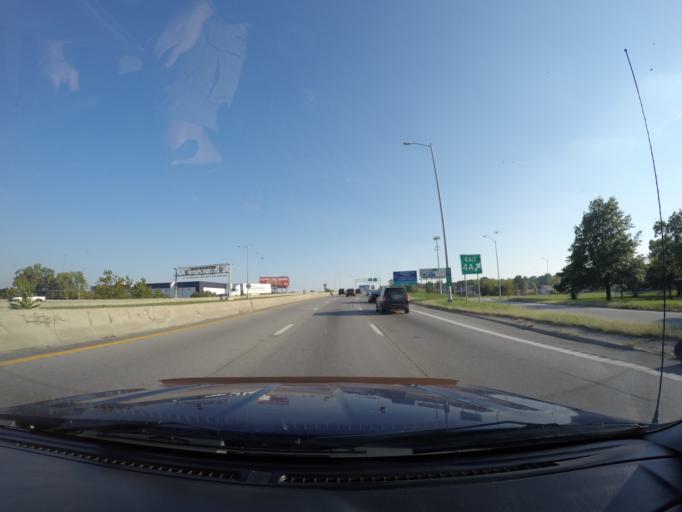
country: US
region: Missouri
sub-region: Jackson County
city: Kansas City
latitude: 39.0941
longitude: -94.5437
